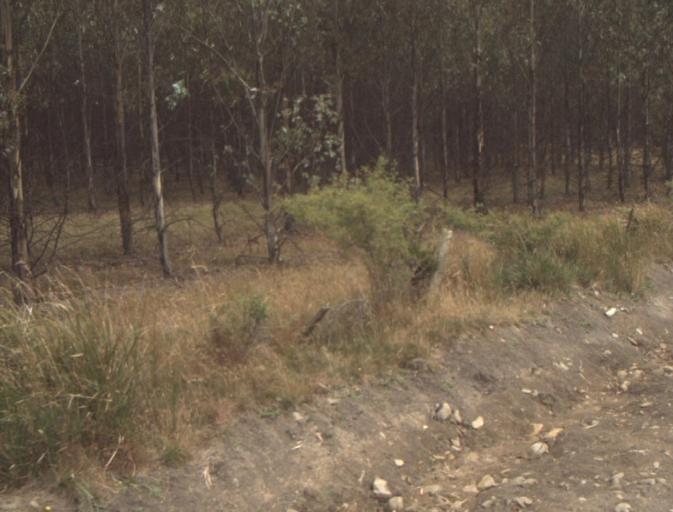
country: AU
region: Tasmania
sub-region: Northern Midlands
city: Evandale
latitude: -41.4527
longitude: 147.4433
